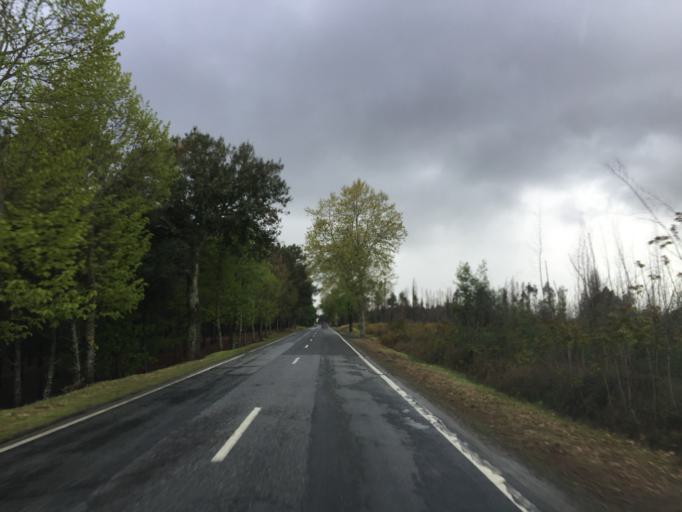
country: PT
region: Guarda
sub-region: Seia
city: Seia
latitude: 40.3925
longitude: -7.7468
